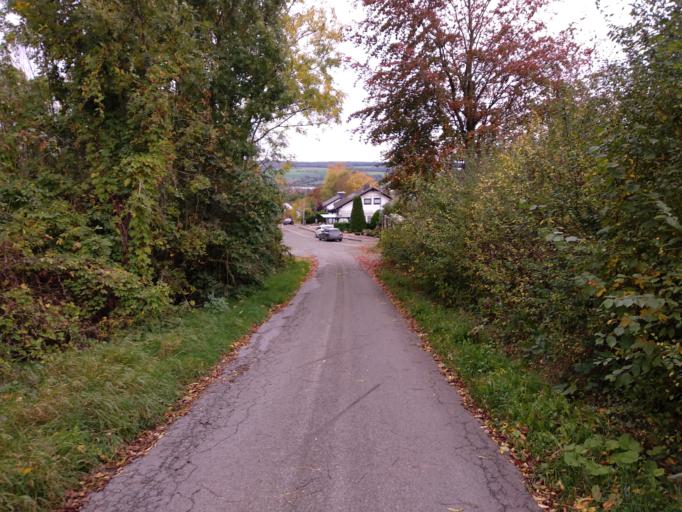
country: DE
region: North Rhine-Westphalia
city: Beverungen
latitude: 51.6632
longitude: 9.3580
